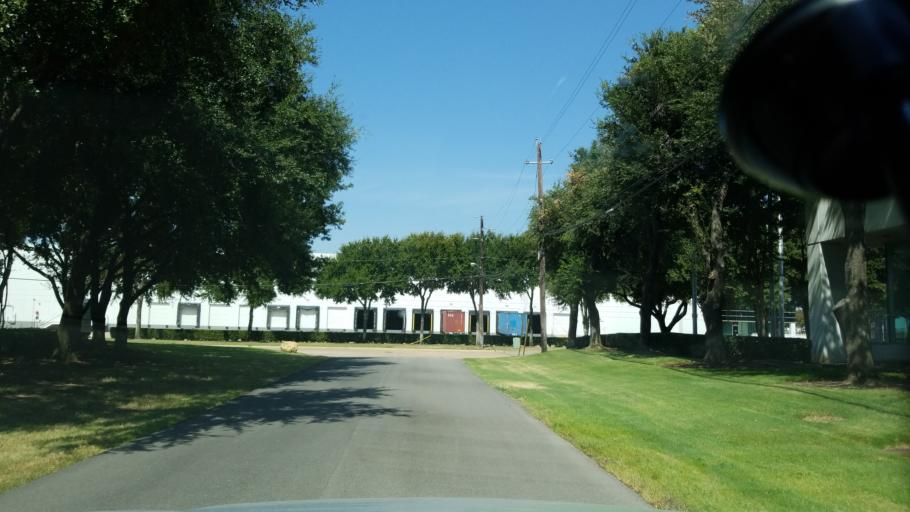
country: US
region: Texas
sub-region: Dallas County
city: Farmers Branch
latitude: 32.9059
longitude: -96.9018
